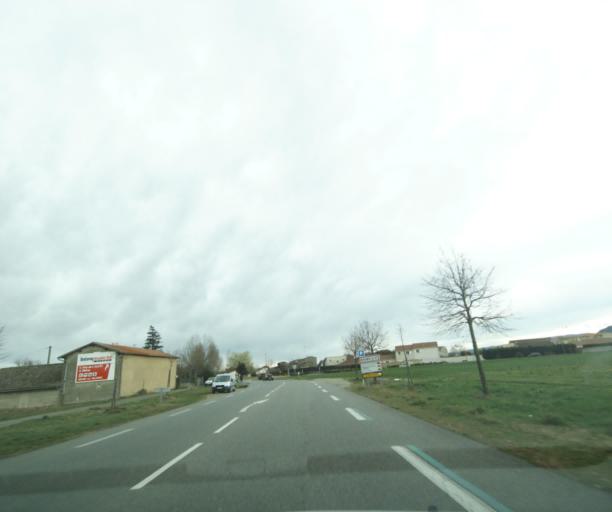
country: FR
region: Rhone-Alpes
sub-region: Departement de la Drome
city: Bourg-les-Valence
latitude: 44.9616
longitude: 4.9096
